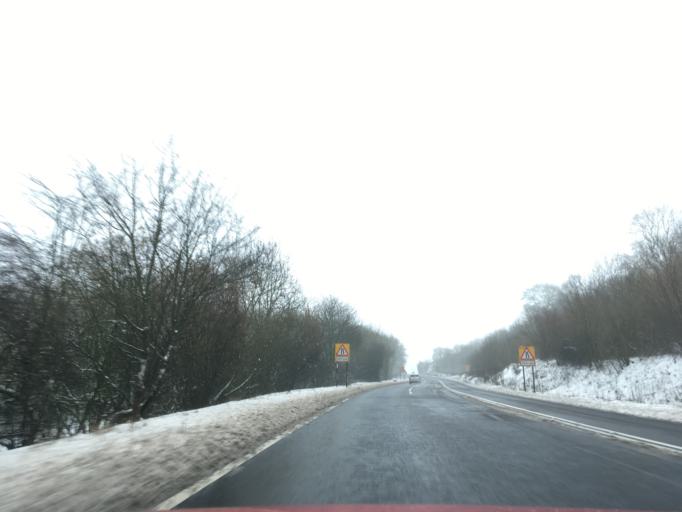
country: GB
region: England
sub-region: Warwickshire
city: Alcester
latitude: 52.2045
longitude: -1.8029
